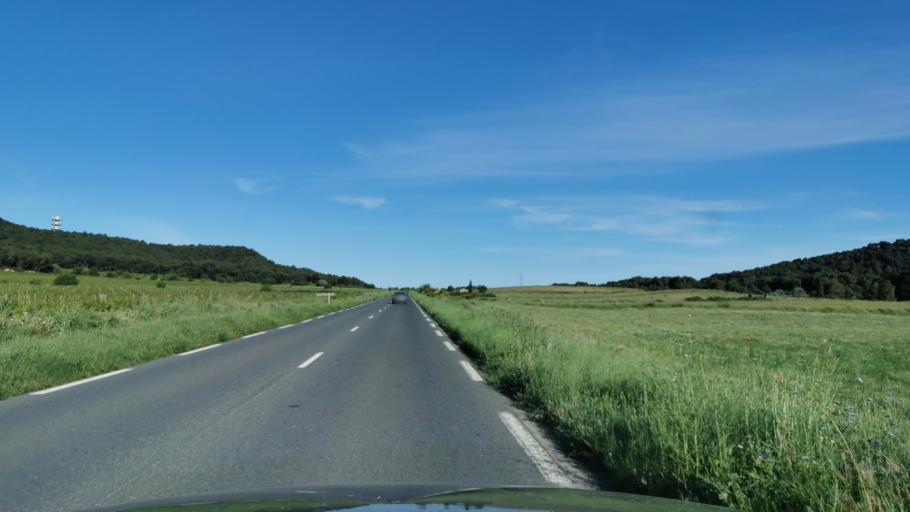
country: FR
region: Languedoc-Roussillon
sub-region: Departement de l'Aude
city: Moussan
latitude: 43.2119
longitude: 2.9398
